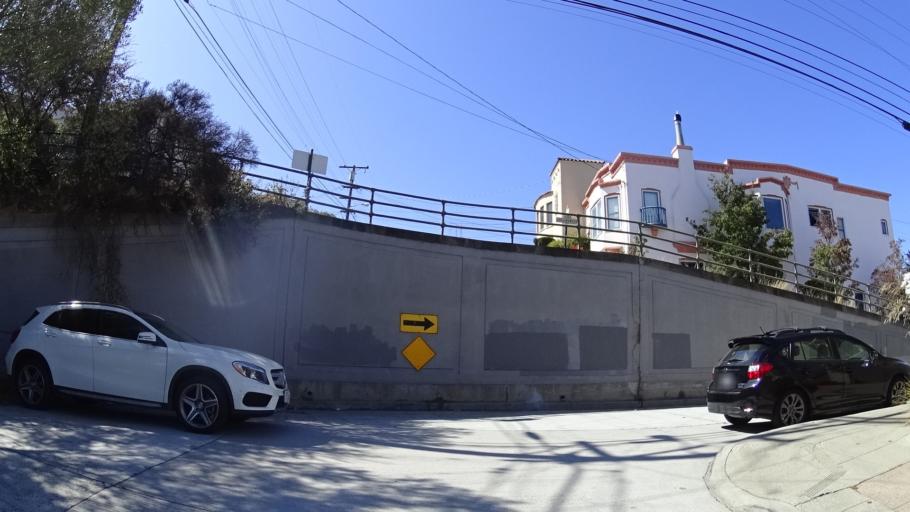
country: US
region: California
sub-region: San Francisco County
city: San Francisco
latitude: 37.7561
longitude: -122.4355
